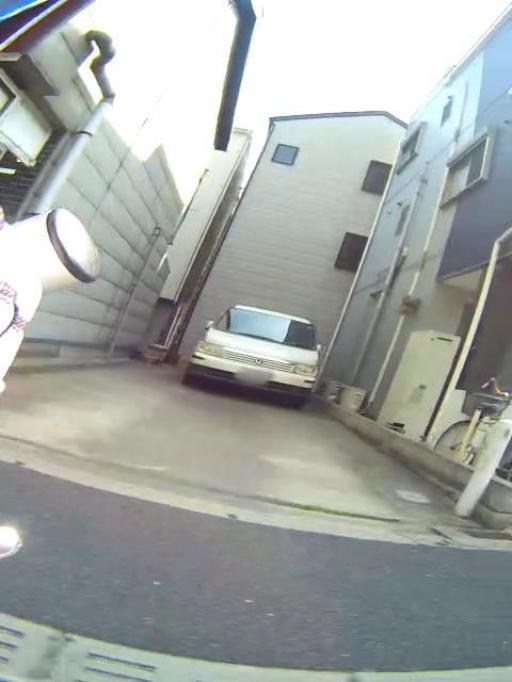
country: JP
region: Osaka
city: Yao
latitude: 34.6214
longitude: 135.5684
